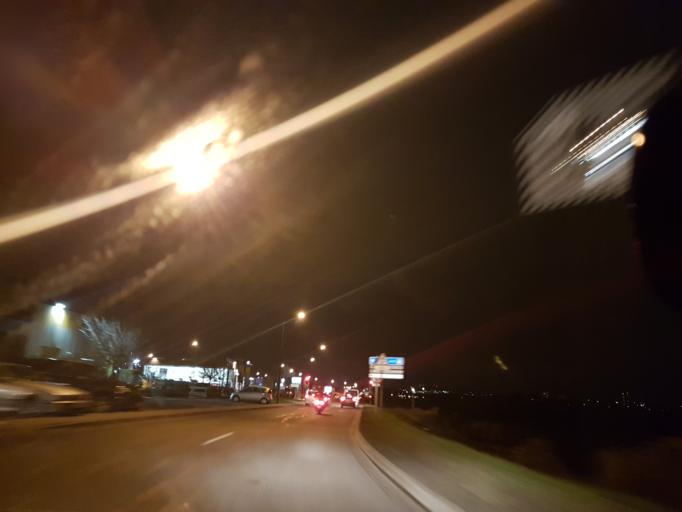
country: FR
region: Ile-de-France
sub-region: Departement des Yvelines
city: Chambourcy
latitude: 48.9068
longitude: 2.0490
